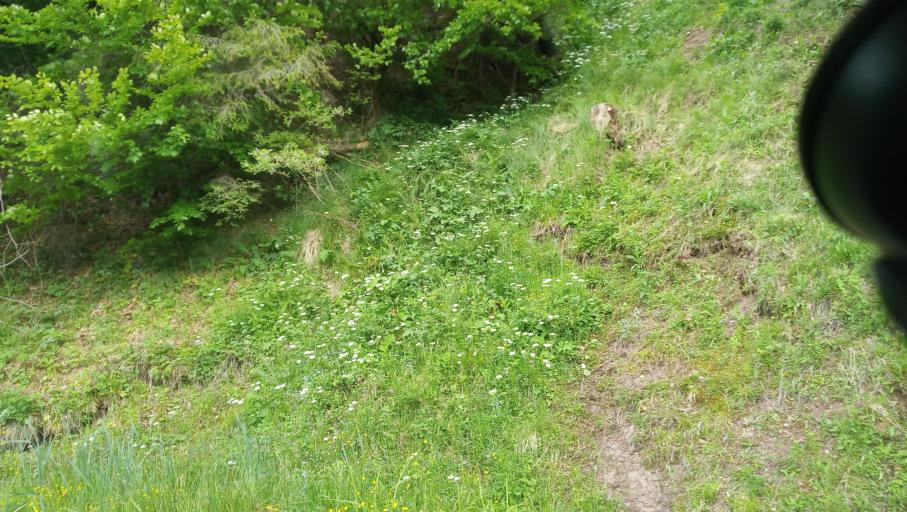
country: RO
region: Alba
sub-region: Comuna Garda de Sus
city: Garda de Sus
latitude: 46.4794
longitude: 22.7984
